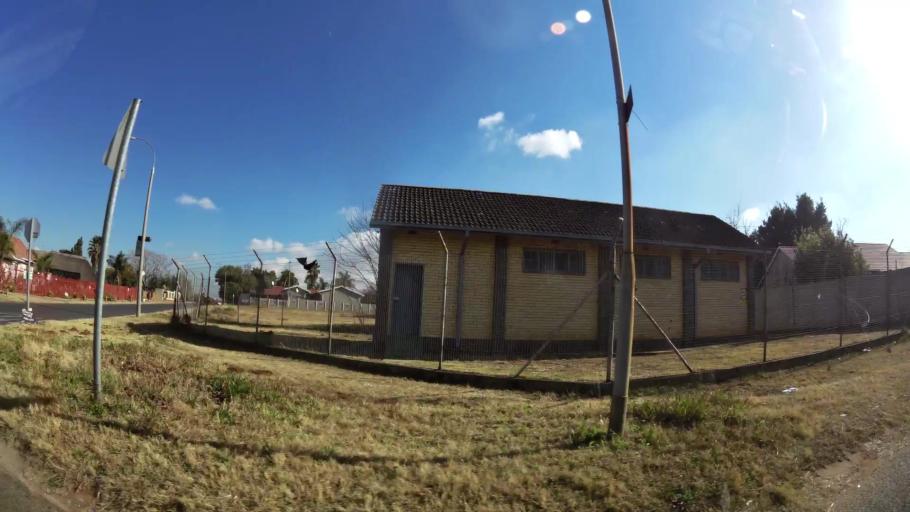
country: ZA
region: Gauteng
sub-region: City of Johannesburg Metropolitan Municipality
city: Roodepoort
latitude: -26.1658
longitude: 27.8227
